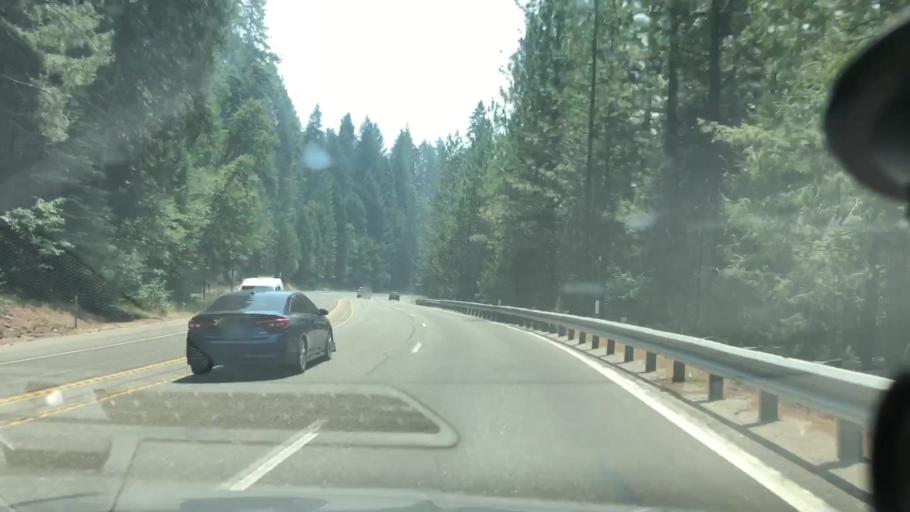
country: US
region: California
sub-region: El Dorado County
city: Pollock Pines
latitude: 38.7662
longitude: -120.5559
